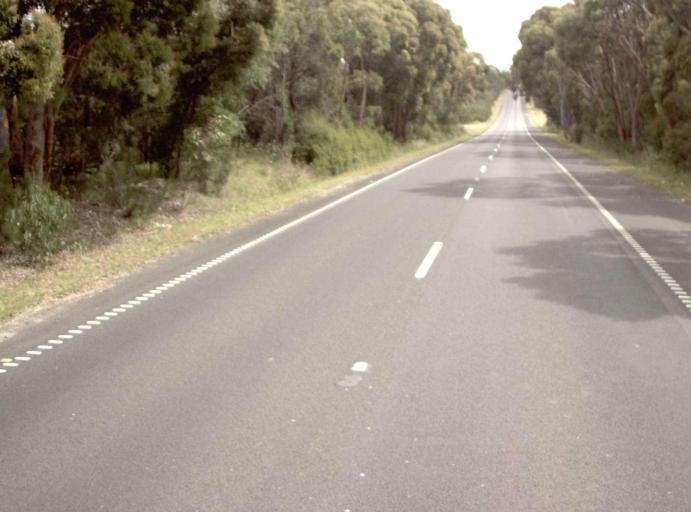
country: AU
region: Victoria
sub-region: Mornington Peninsula
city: Moorooduc
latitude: -38.2191
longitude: 145.1047
